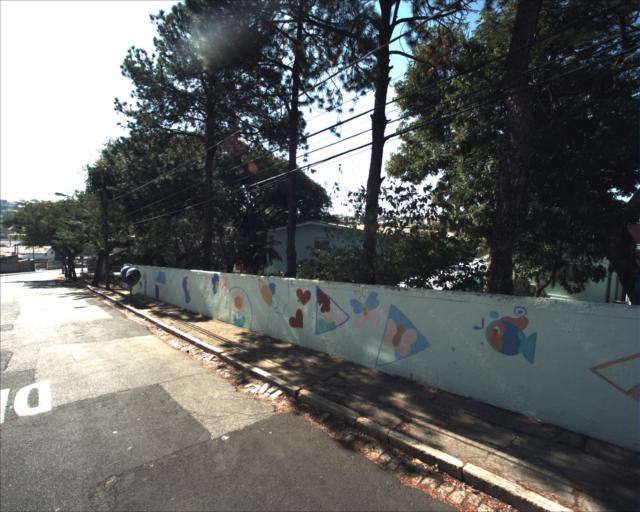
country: BR
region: Sao Paulo
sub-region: Sorocaba
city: Sorocaba
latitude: -23.5092
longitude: -47.4335
